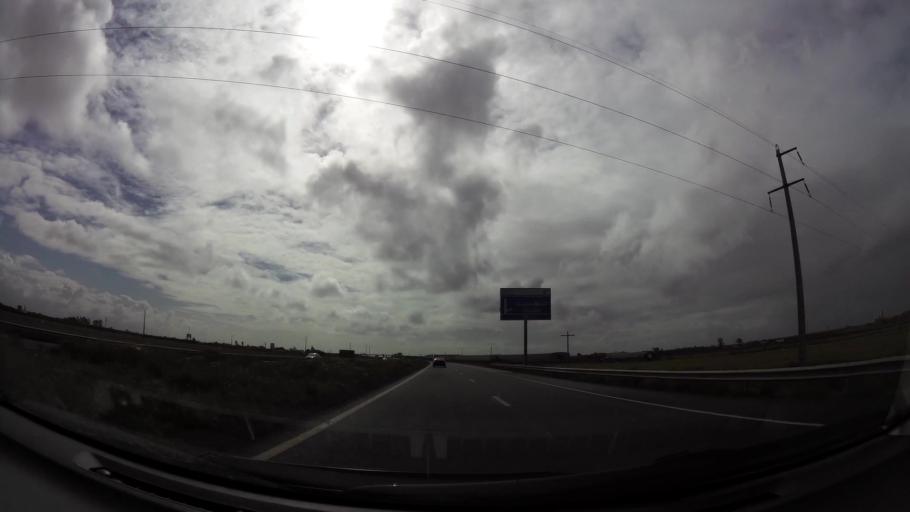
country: MA
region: Grand Casablanca
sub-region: Nouaceur
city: Dar Bouazza
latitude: 33.3531
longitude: -7.9850
